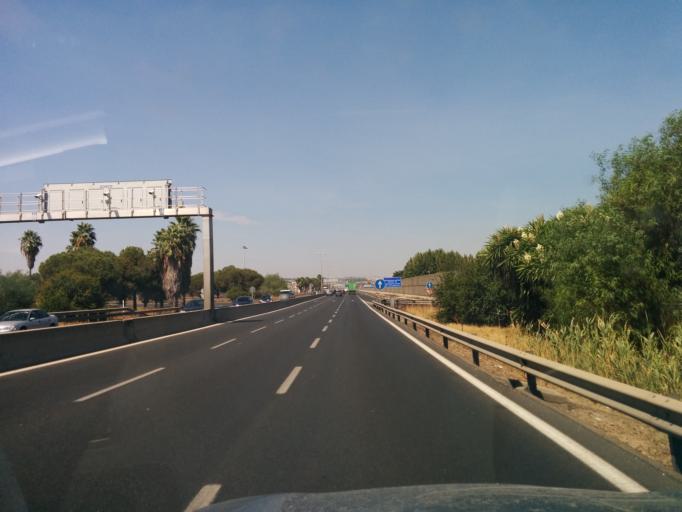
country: ES
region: Andalusia
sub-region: Provincia de Sevilla
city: Gelves
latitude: 37.3587
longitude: -6.0046
